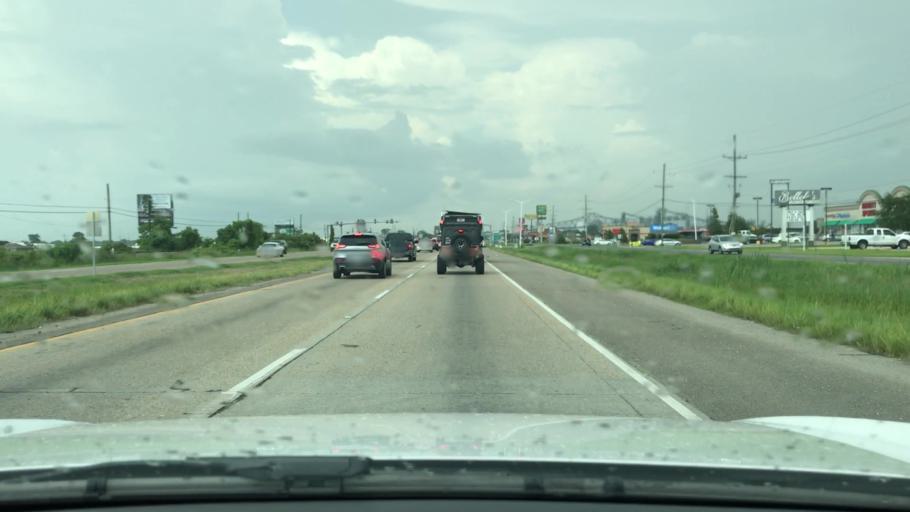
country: US
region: Louisiana
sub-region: West Baton Rouge Parish
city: Port Allen
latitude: 30.4198
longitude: -91.2204
